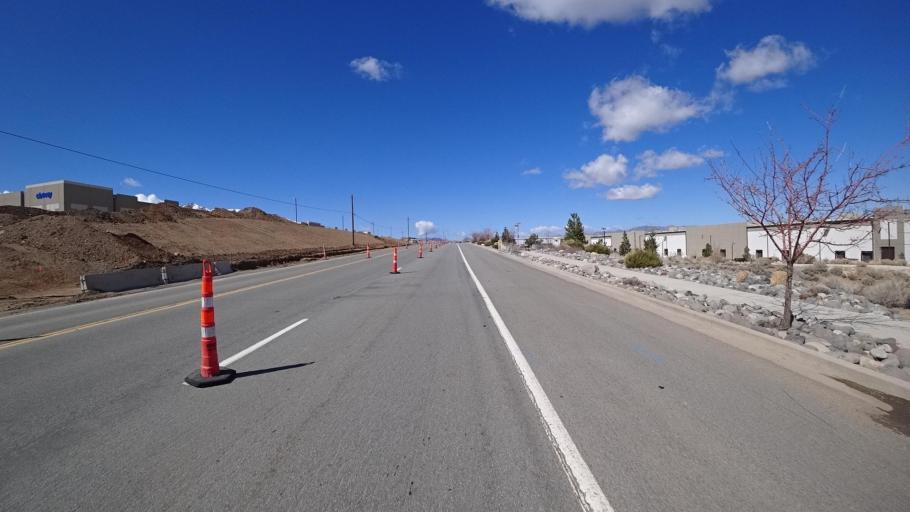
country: US
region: Nevada
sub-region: Washoe County
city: Golden Valley
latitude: 39.6012
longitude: -119.8473
